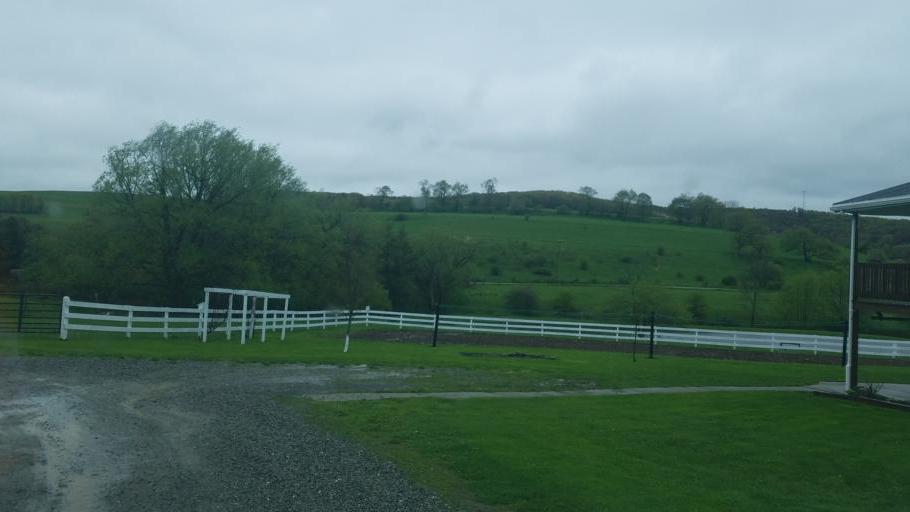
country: US
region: Pennsylvania
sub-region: Potter County
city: Galeton
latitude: 41.9095
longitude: -77.7721
